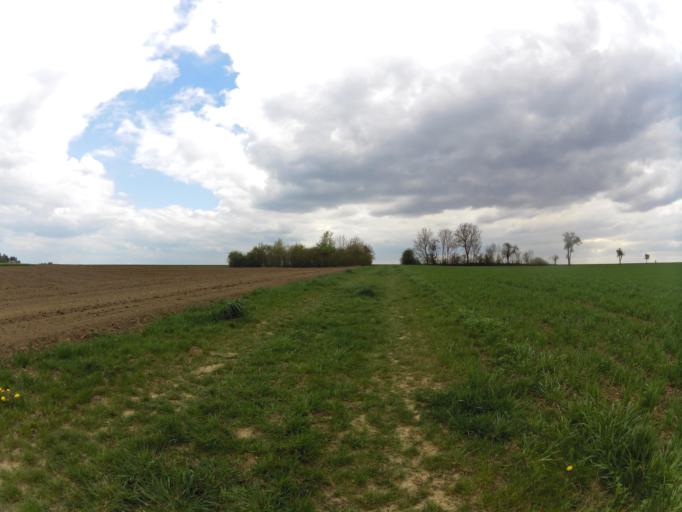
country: DE
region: Bavaria
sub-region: Regierungsbezirk Unterfranken
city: Giebelstadt
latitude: 49.6502
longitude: 9.9372
